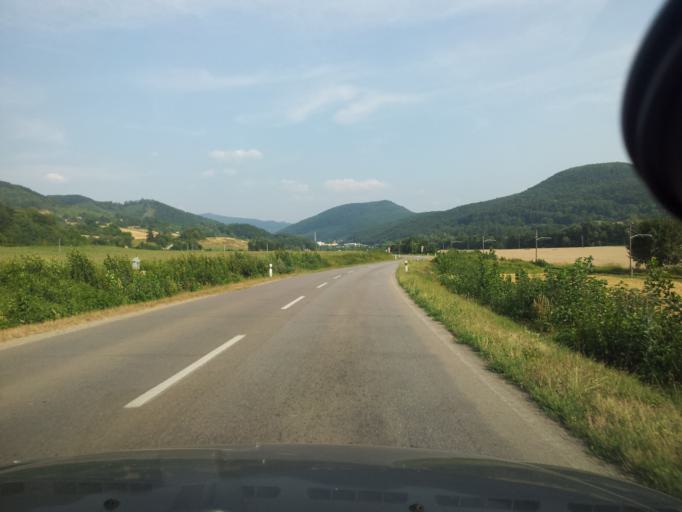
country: SK
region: Trenciansky
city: Nova Dubnica
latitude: 48.9250
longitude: 18.1384
